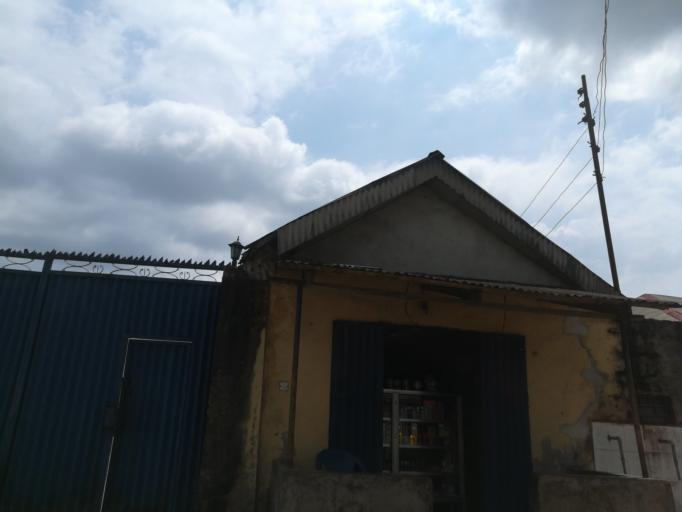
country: NG
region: Rivers
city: Okrika
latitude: 4.7307
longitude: 7.1492
